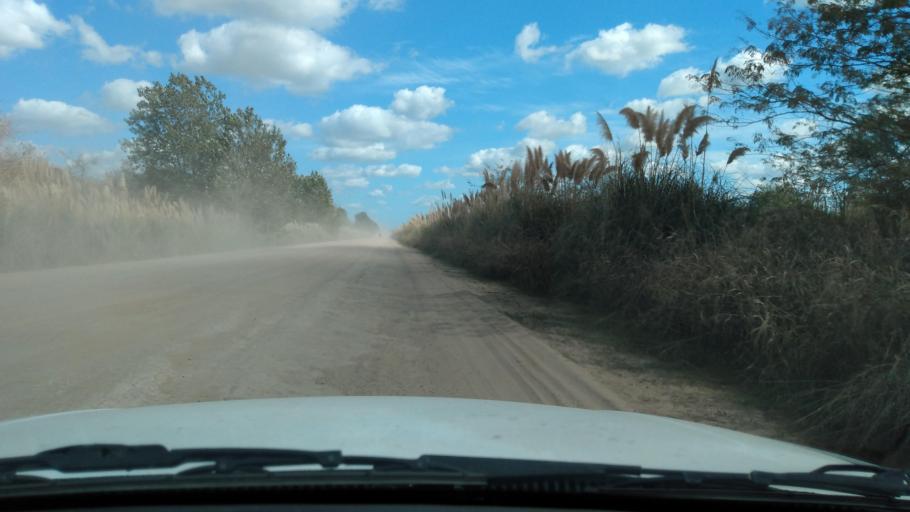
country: AR
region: Buenos Aires
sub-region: Partido de Navarro
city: Navarro
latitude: -34.9994
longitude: -59.3339
